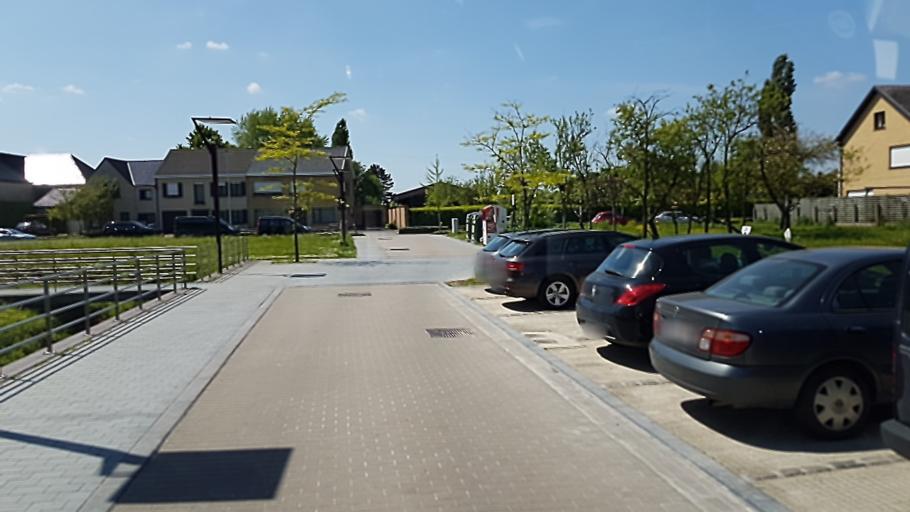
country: BE
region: Flanders
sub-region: Provincie West-Vlaanderen
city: Zedelgem
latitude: 51.1425
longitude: 3.1354
